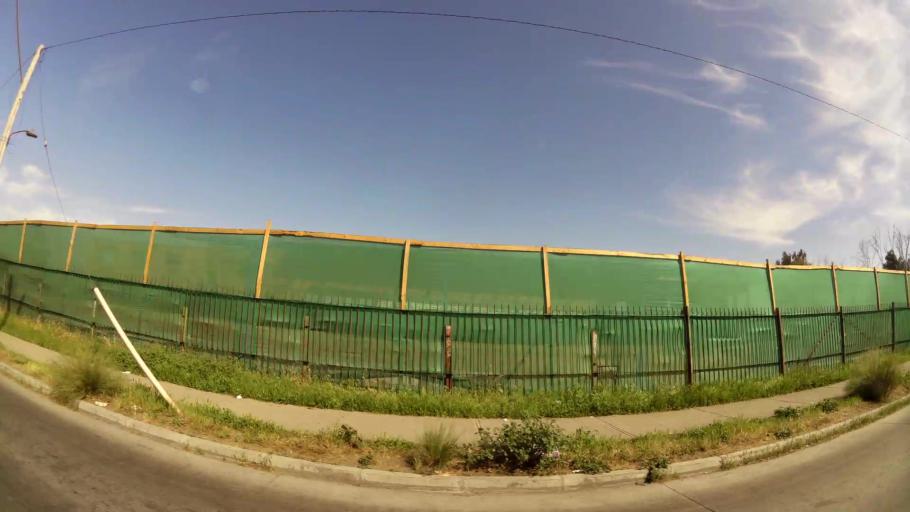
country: CL
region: Santiago Metropolitan
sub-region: Provincia de Santiago
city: Villa Presidente Frei, Nunoa, Santiago, Chile
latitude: -33.4509
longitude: -70.5400
